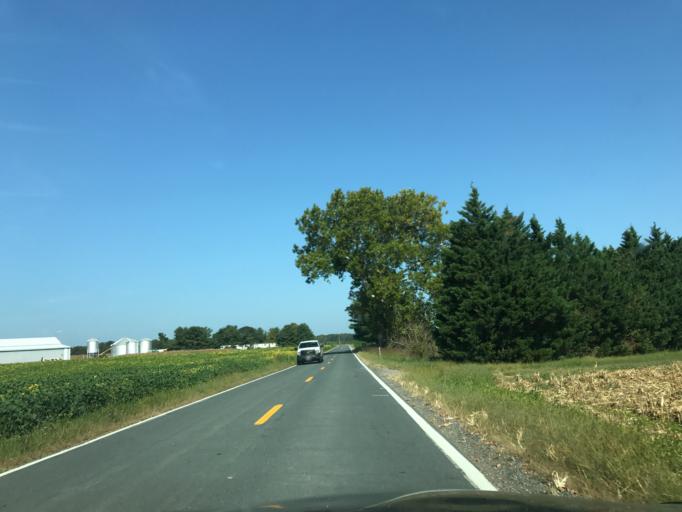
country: US
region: Maryland
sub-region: Queen Anne's County
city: Kingstown
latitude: 39.3342
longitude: -75.9527
